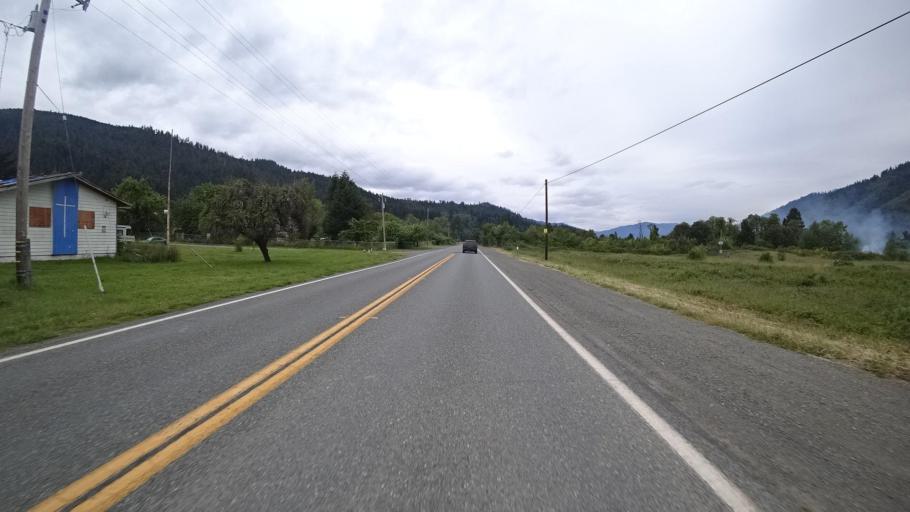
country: US
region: California
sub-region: Humboldt County
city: Willow Creek
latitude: 41.0288
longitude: -123.6600
